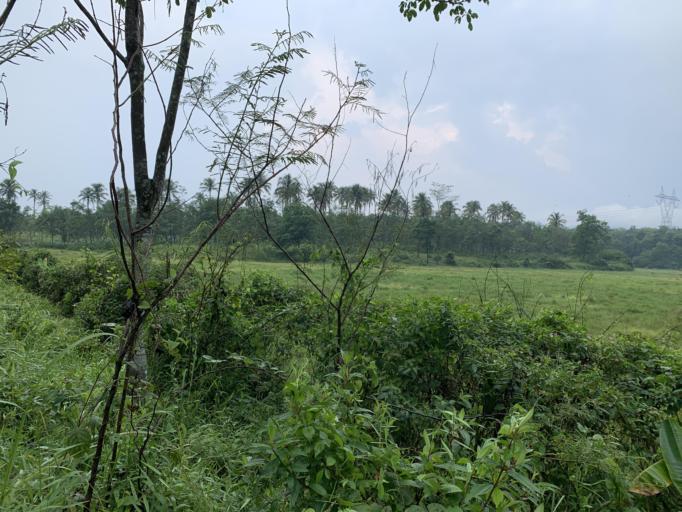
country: ID
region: West Java
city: Parung
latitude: -6.4192
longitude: 106.6290
